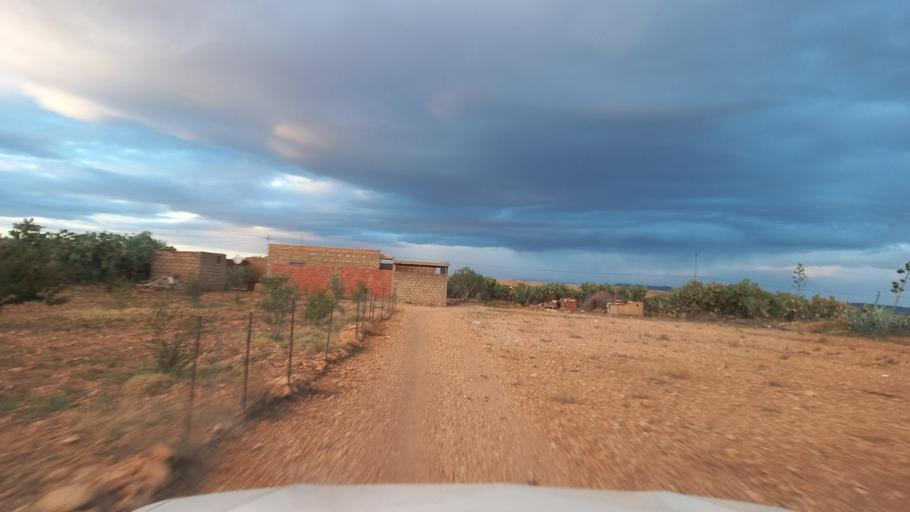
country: TN
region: Al Qasrayn
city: Kasserine
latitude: 35.2617
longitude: 8.9388
